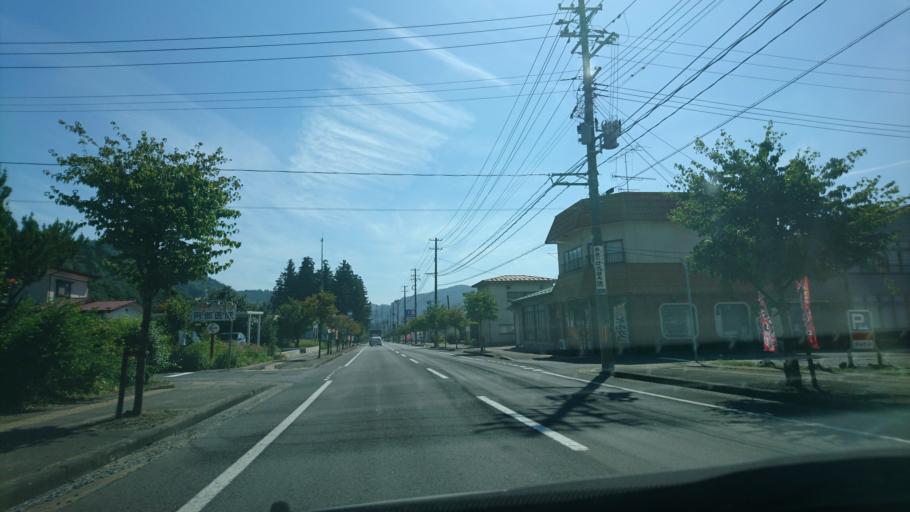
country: JP
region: Iwate
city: Ichinoseki
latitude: 38.9912
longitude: 141.2538
